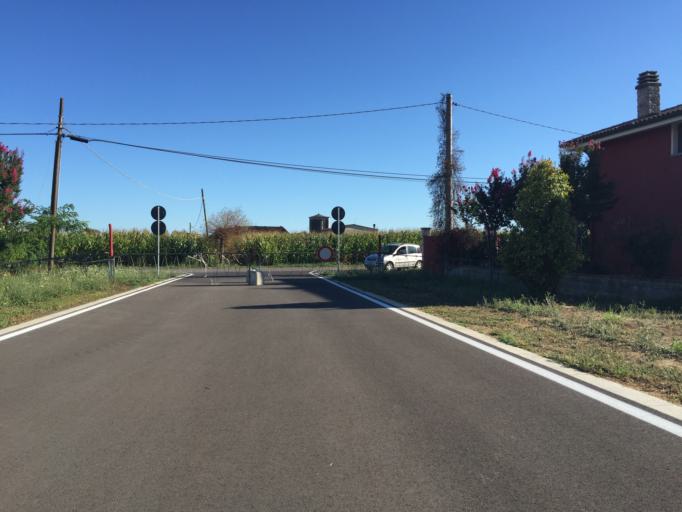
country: IT
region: Tuscany
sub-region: Provincia di Pistoia
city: Anchione
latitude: 43.8374
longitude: 10.7662
